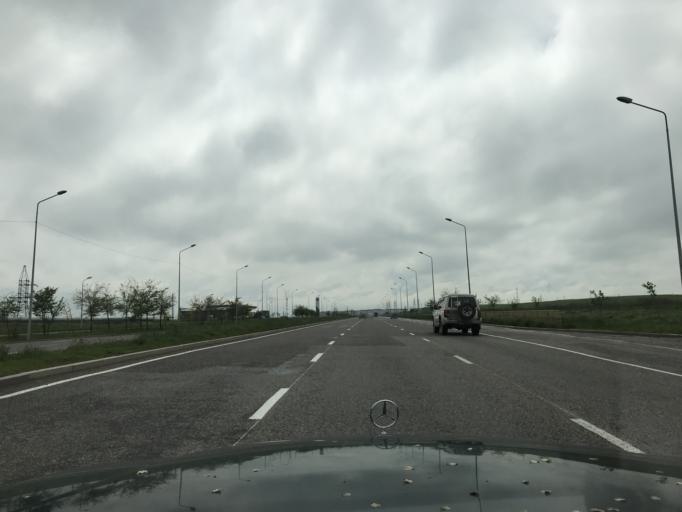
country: KZ
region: Almaty Oblysy
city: Burunday
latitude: 43.2976
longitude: 76.8339
